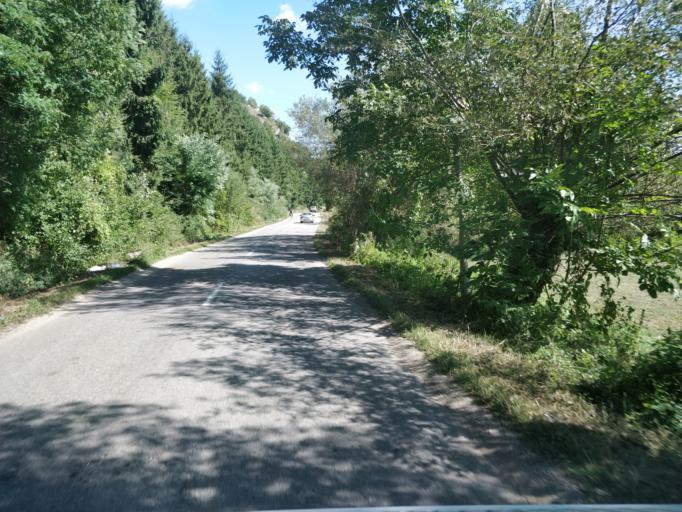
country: RO
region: Cluj
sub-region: Comuna Sacueu
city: Sacuieu
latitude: 46.8707
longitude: 22.8758
